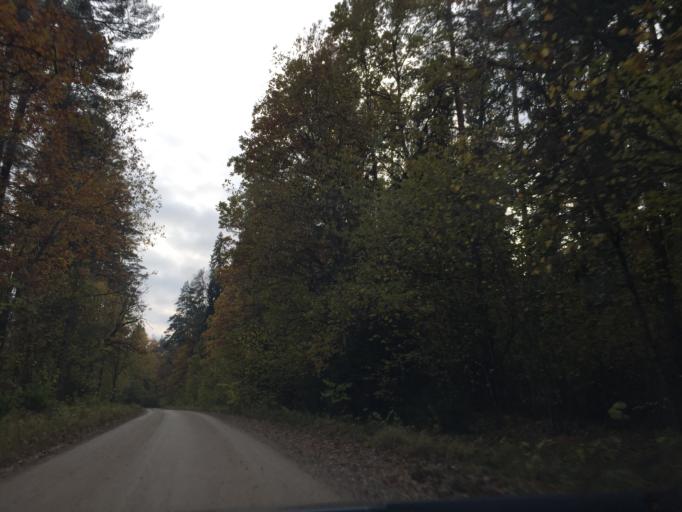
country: LV
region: Cesu Rajons
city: Cesis
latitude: 57.3551
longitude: 25.1702
